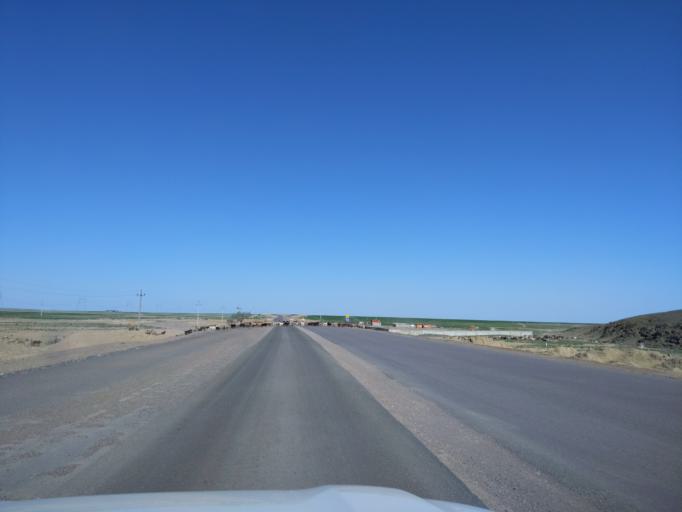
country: KZ
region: Almaty Oblysy
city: Bakanas
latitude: 44.0944
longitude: 75.9866
